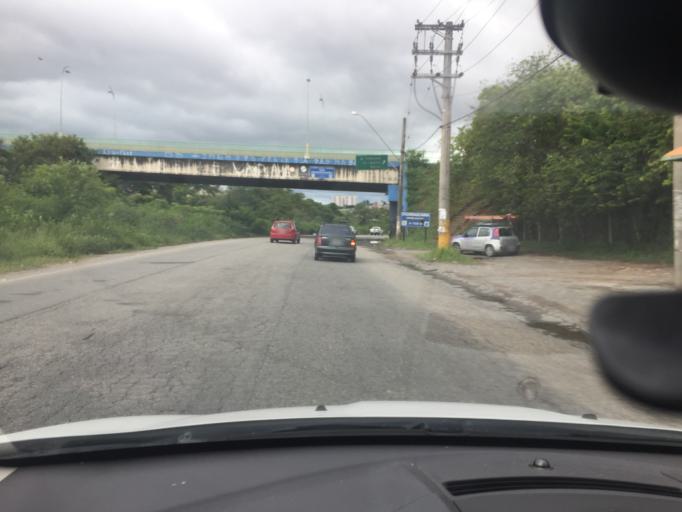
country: BR
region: Sao Paulo
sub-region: Varzea Paulista
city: Varzea Paulista
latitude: -23.2083
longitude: -46.8317
